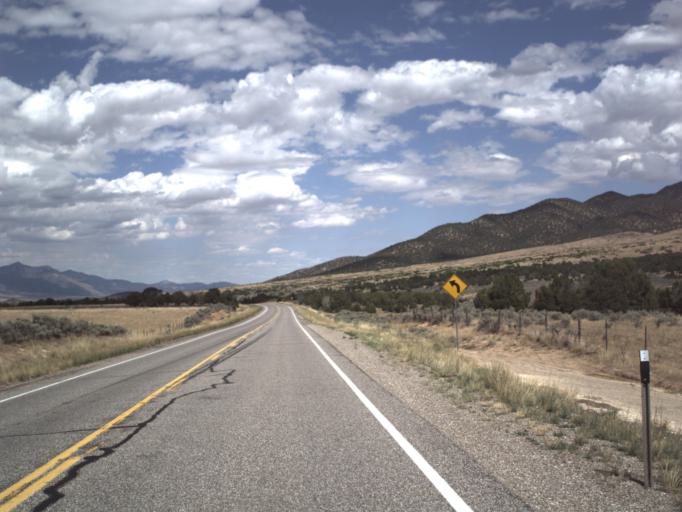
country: US
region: Utah
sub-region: Sanpete County
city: Centerfield
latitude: 39.1419
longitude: -112.0622
